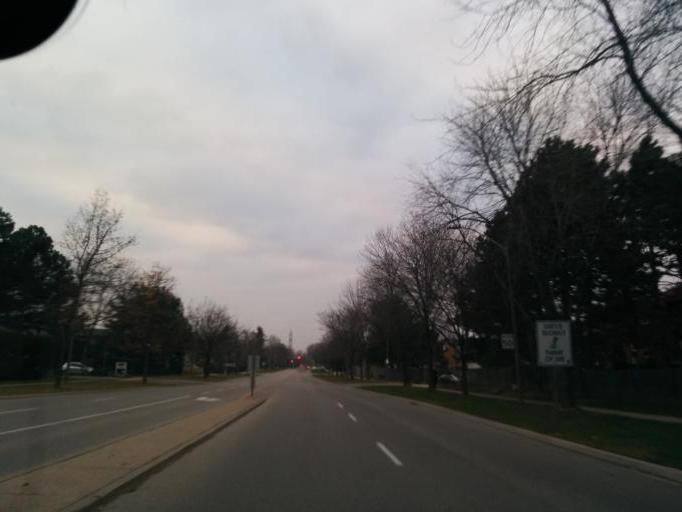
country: CA
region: Ontario
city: Etobicoke
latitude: 43.6333
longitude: -79.6009
